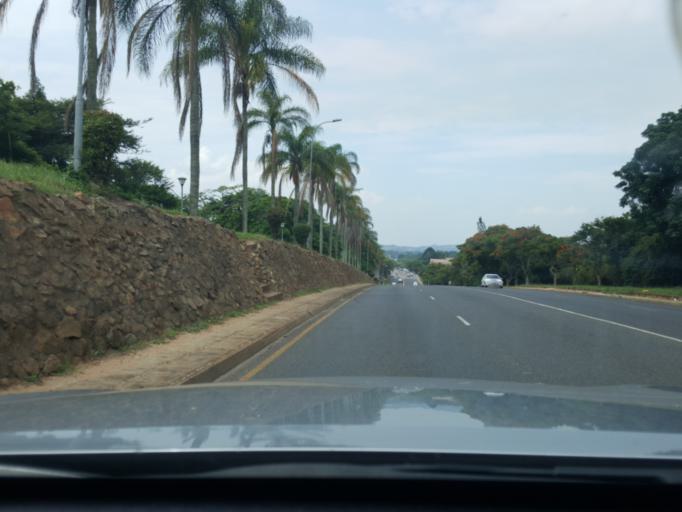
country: ZA
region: Mpumalanga
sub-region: Ehlanzeni District
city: White River
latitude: -25.3334
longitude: 31.0068
